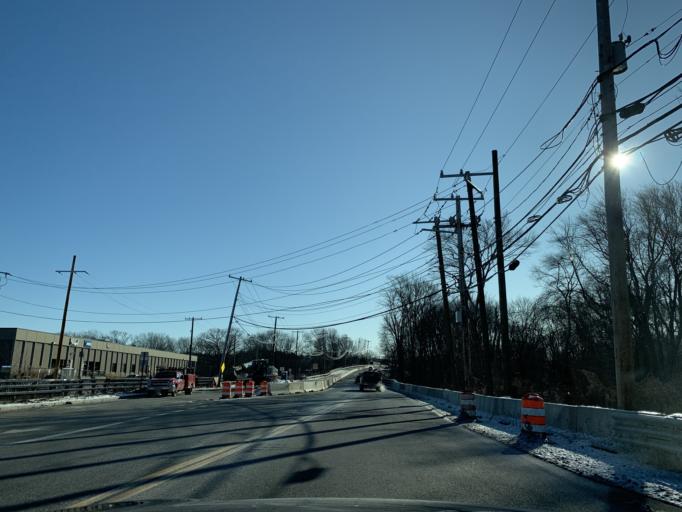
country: US
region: Massachusetts
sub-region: Norfolk County
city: Canton
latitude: 42.1981
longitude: -71.1568
